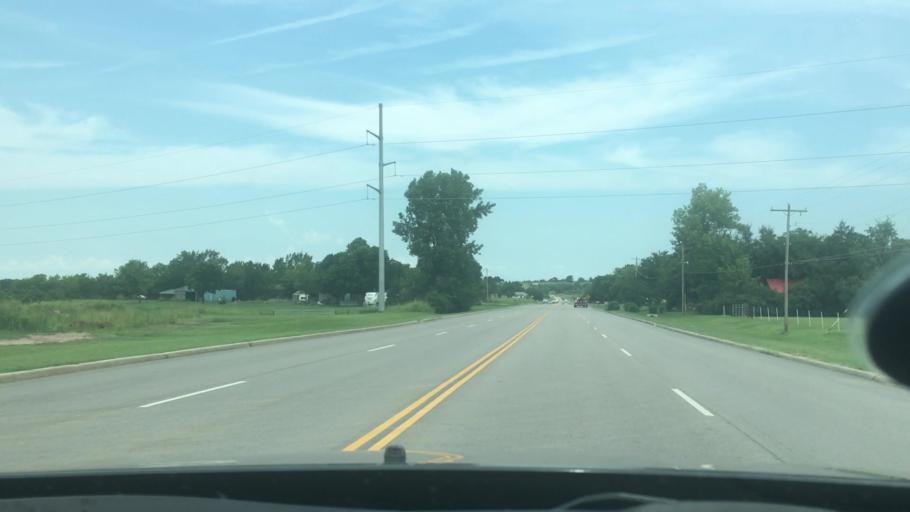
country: US
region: Oklahoma
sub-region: Seminole County
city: Seminole
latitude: 35.2626
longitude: -96.7145
